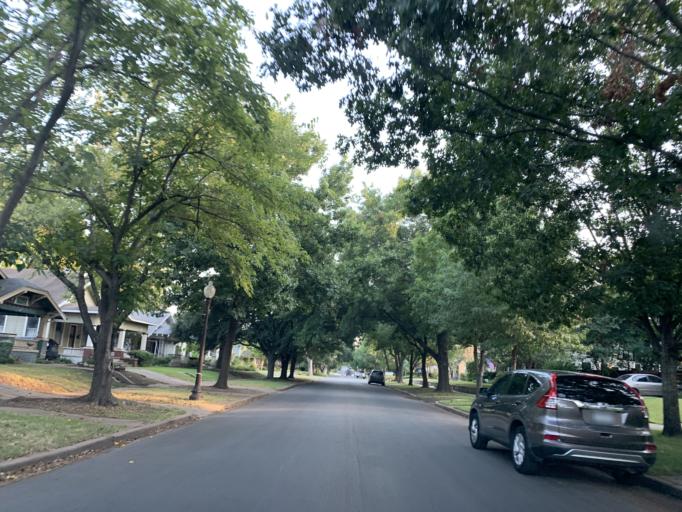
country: US
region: Texas
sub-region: Dallas County
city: Cockrell Hill
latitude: 32.7473
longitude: -96.8465
